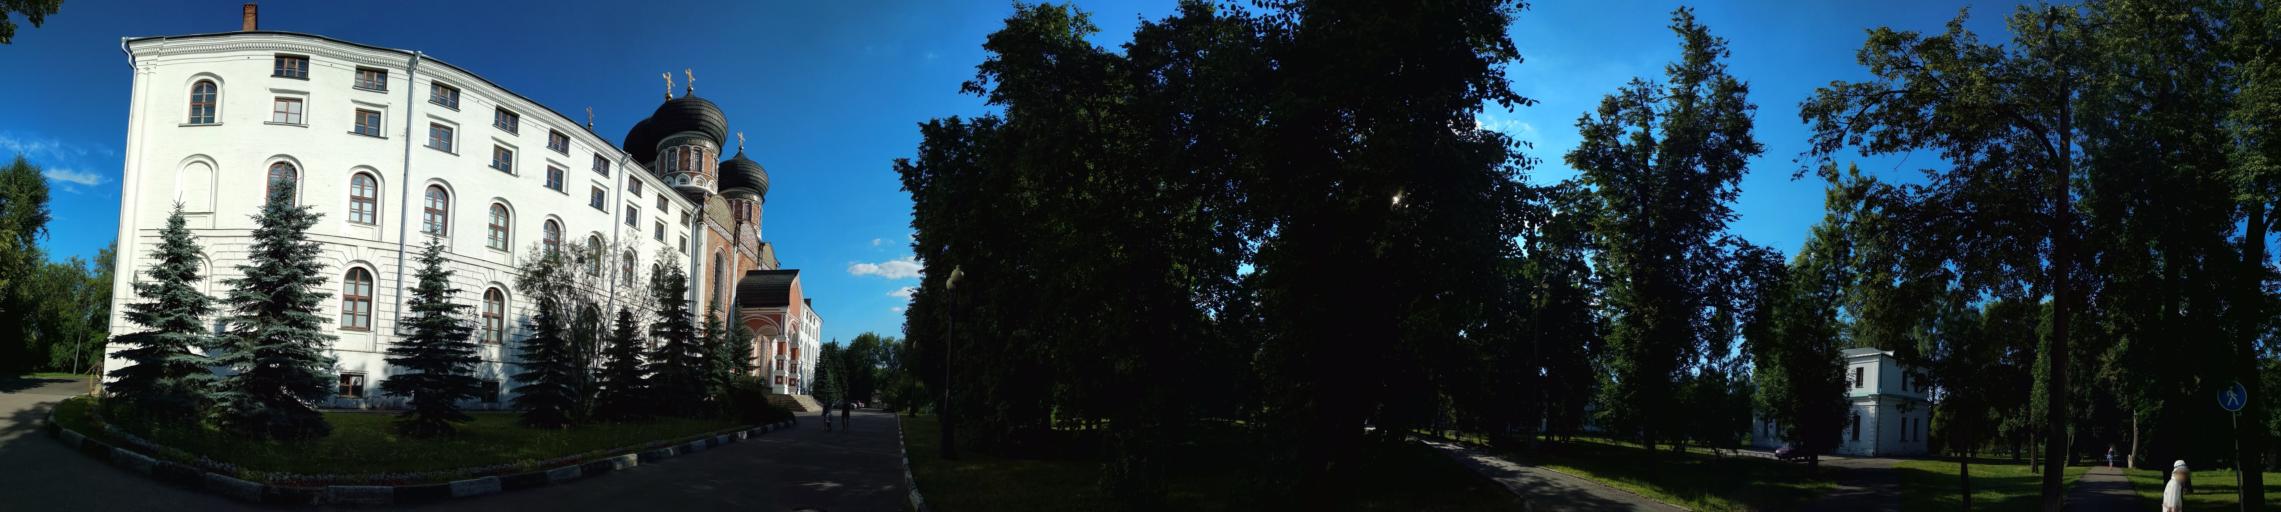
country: RU
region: Moscow
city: Metrogorodok
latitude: 55.7918
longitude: 37.7649
